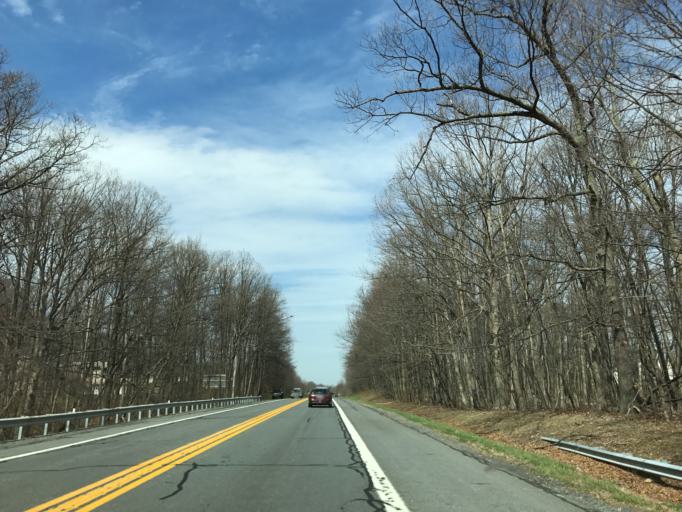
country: US
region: Maryland
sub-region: Frederick County
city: Jefferson
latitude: 39.3445
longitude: -77.5070
